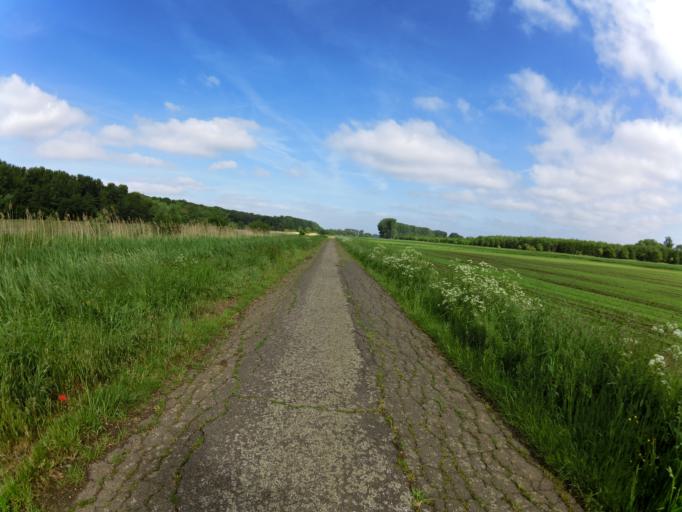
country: DE
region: North Rhine-Westphalia
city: Huckelhoven
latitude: 51.0219
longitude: 6.2081
